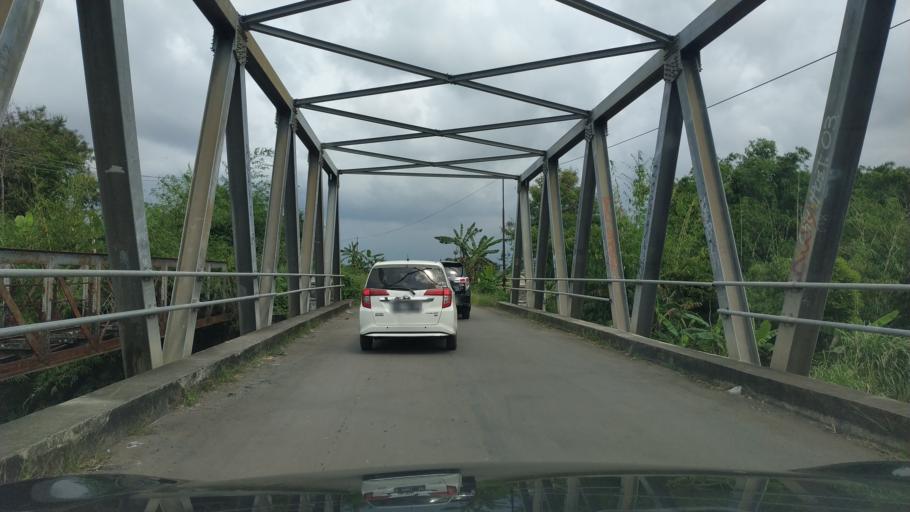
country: ID
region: Central Java
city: Pemalang
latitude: -6.9199
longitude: 109.3301
